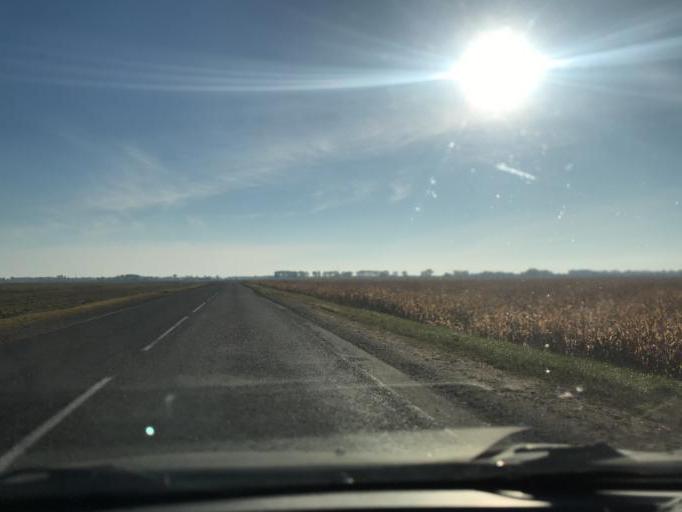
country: BY
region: Gomel
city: Brahin
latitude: 51.7816
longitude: 30.2236
